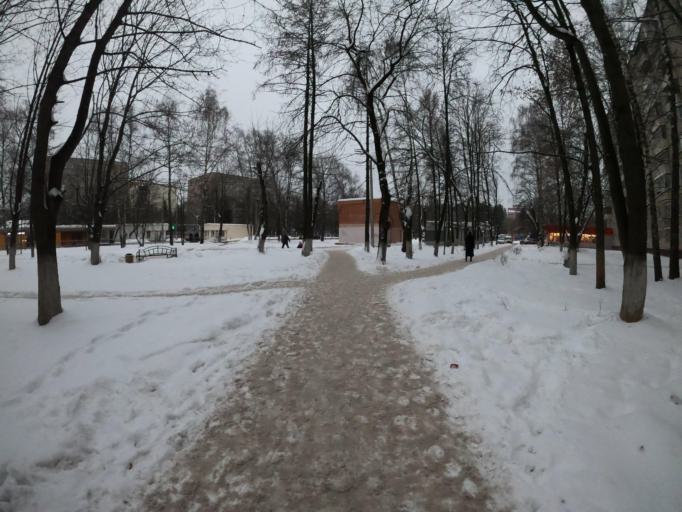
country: RU
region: Moskovskaya
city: Dubrovitsy
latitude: 55.4211
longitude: 37.5082
